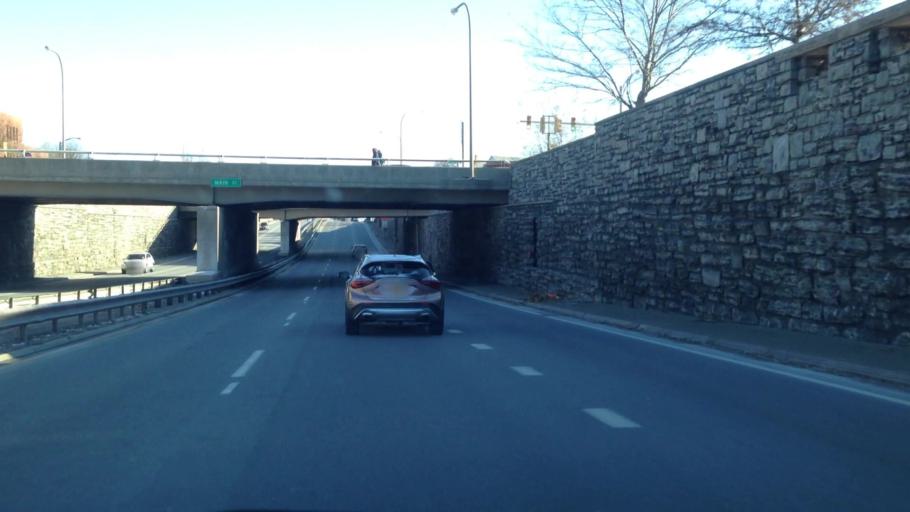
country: US
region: New York
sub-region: Erie County
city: Kenmore
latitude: 42.9283
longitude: -78.8518
